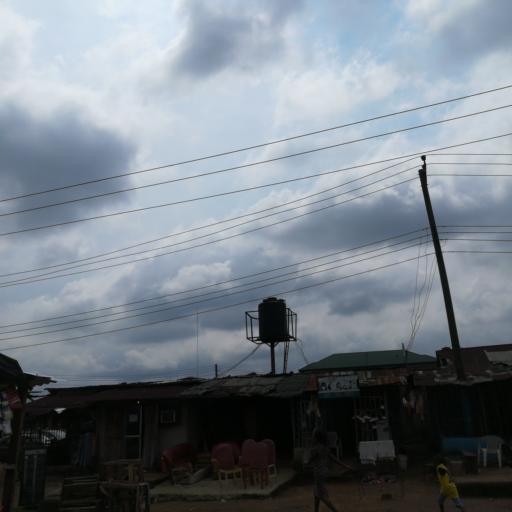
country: NG
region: Rivers
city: Port Harcourt
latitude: 4.8421
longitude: 7.0684
